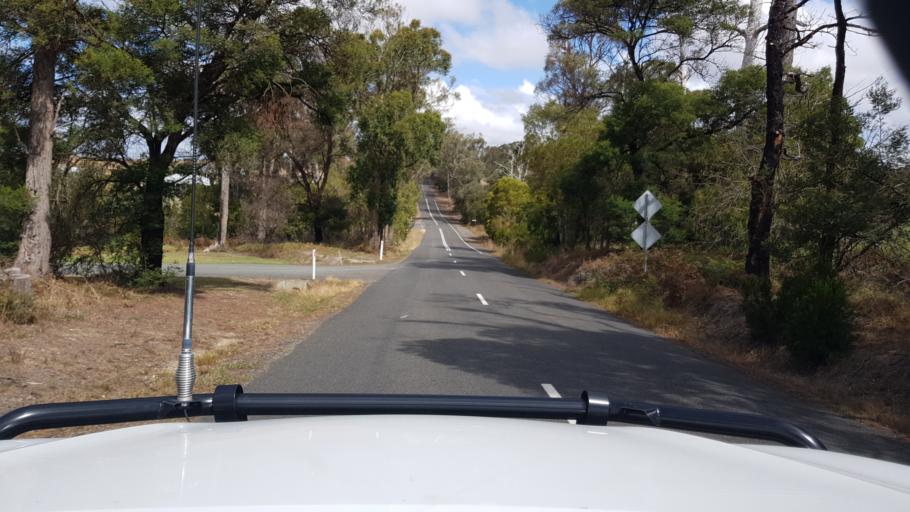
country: AU
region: Victoria
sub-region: East Gippsland
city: Bairnsdale
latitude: -37.7772
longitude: 147.6041
